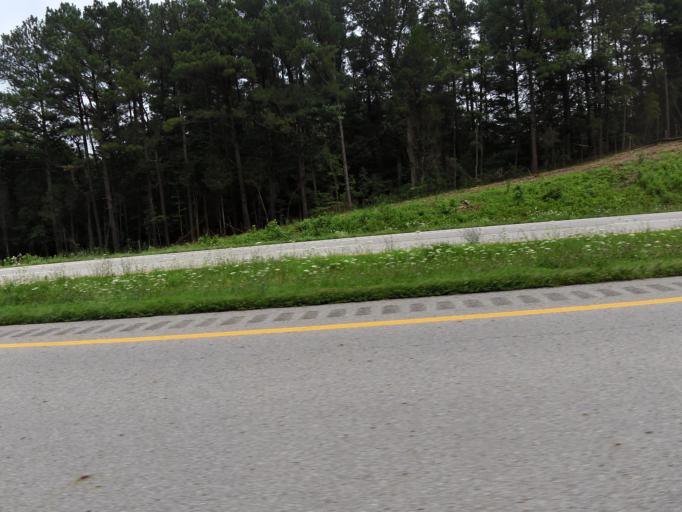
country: US
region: Kentucky
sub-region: Ohio County
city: Beaver Dam
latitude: 37.3540
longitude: -86.9104
